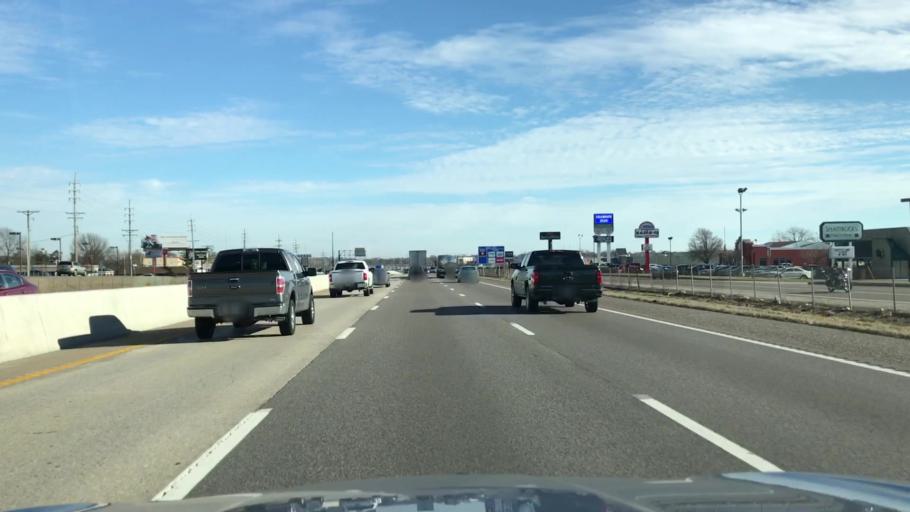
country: US
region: Missouri
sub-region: Saint Charles County
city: Saint Peters
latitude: 38.7963
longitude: -90.5751
